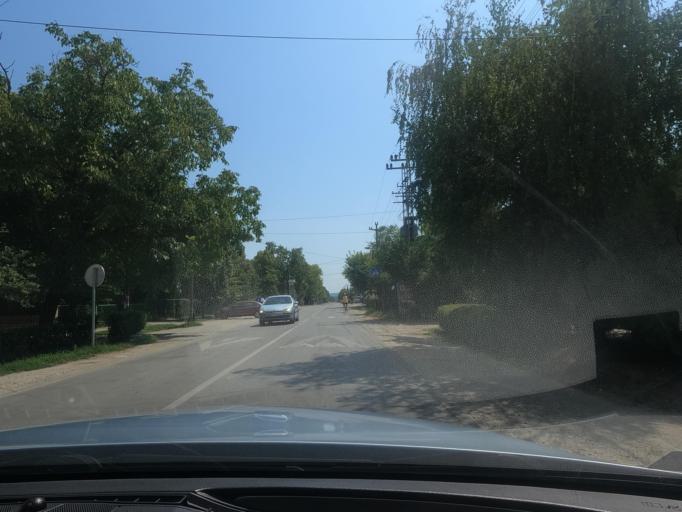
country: RS
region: Autonomna Pokrajina Vojvodina
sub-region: Juznobacki Okrug
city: Kovilj
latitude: 45.2257
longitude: 20.0212
